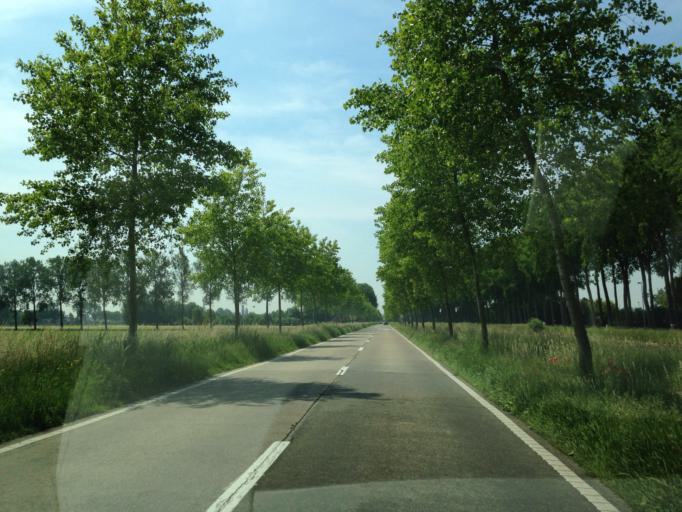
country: BE
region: Flanders
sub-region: Provincie West-Vlaanderen
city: Sint-Kruis
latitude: 51.2307
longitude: 3.2526
